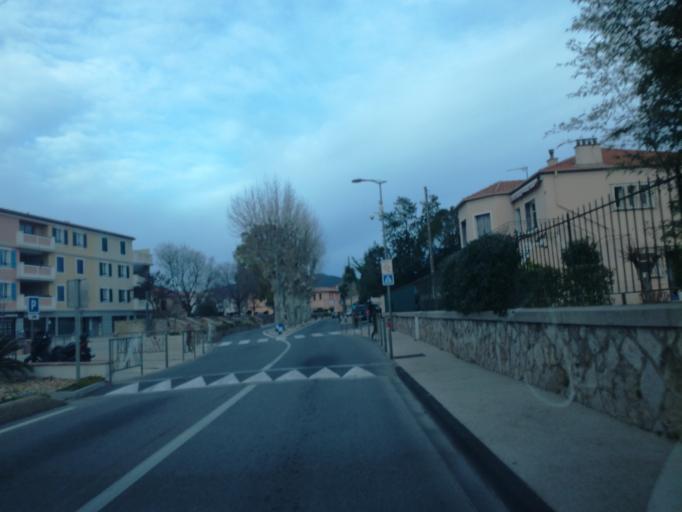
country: FR
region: Provence-Alpes-Cote d'Azur
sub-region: Departement du Var
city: La Crau
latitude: 43.1470
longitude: 6.0769
